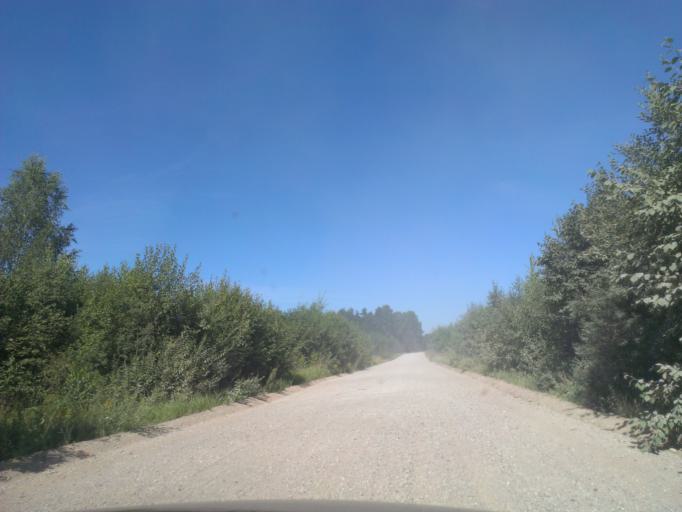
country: LV
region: Malpils
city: Malpils
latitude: 57.0509
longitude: 25.1199
